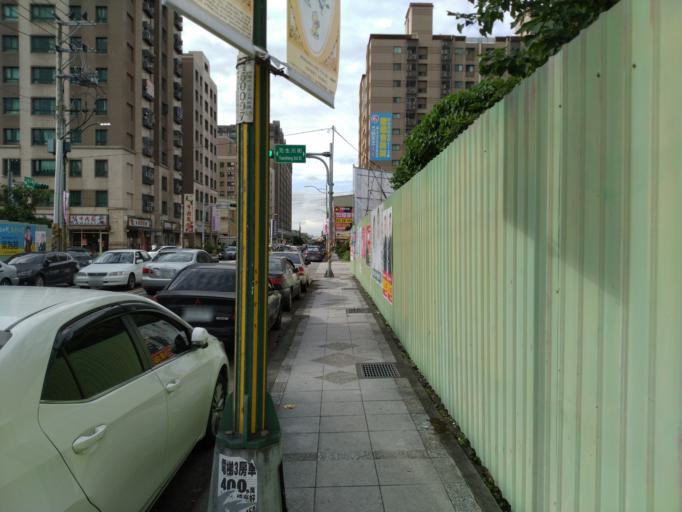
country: TW
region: Taiwan
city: Taoyuan City
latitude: 24.9769
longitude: 121.2522
